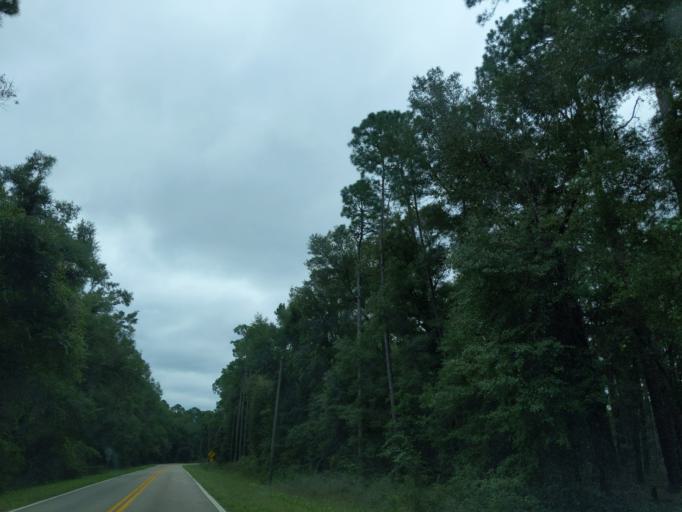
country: US
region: Florida
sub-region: Gadsden County
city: Midway
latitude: 30.4071
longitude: -84.4159
